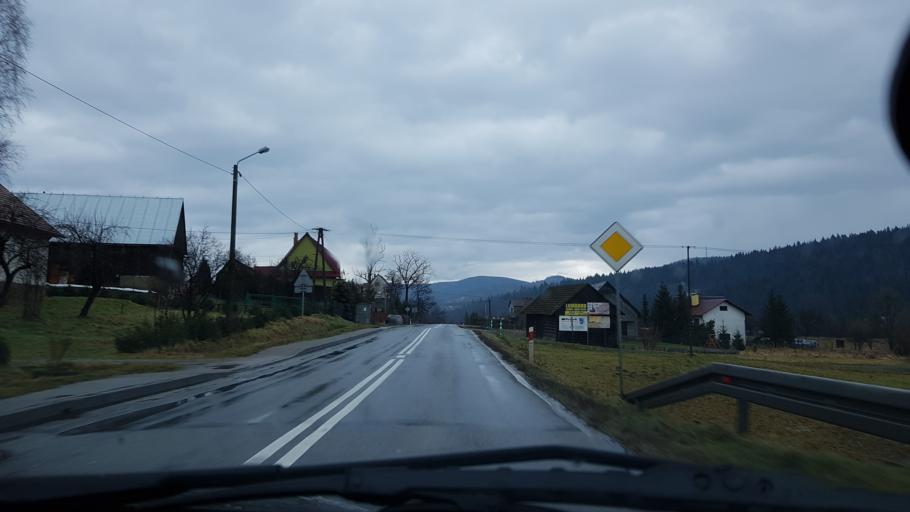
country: PL
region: Lesser Poland Voivodeship
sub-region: Powiat suski
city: Kukow
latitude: 49.7327
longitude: 19.4834
